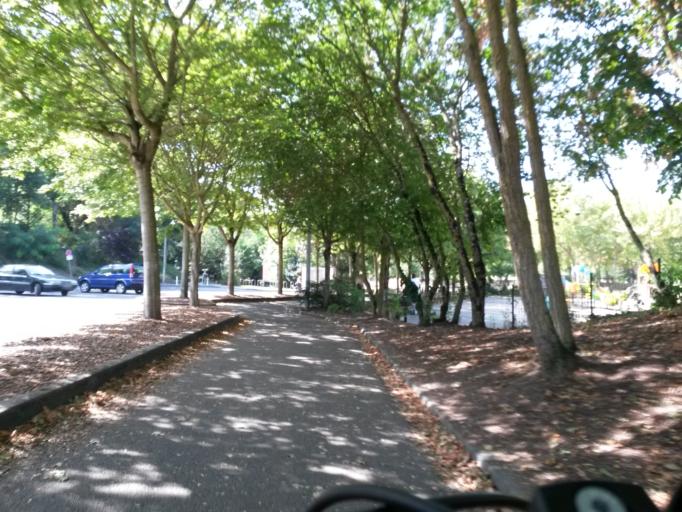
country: FR
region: Poitou-Charentes
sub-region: Departement de la Charente-Maritime
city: La Rochelle
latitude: 46.1655
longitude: -1.1558
